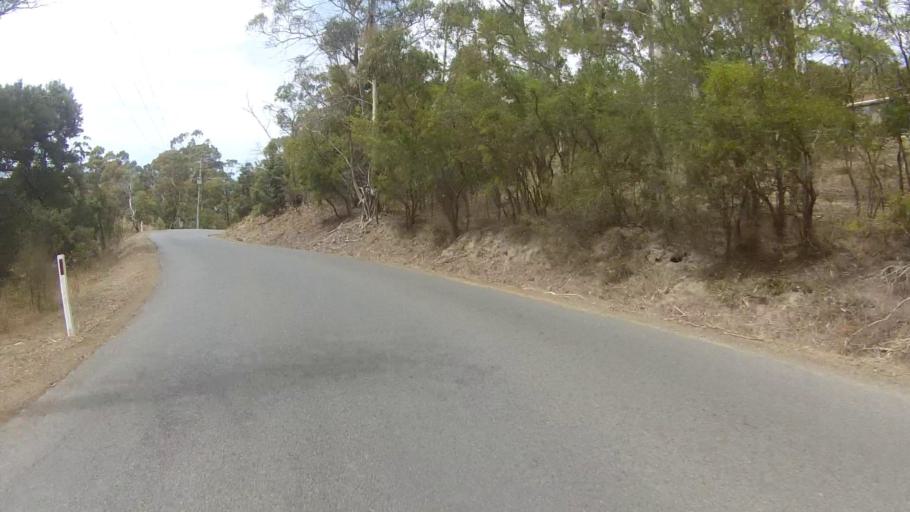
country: AU
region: Tasmania
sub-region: Kingborough
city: Blackmans Bay
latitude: -43.0356
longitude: 147.3320
